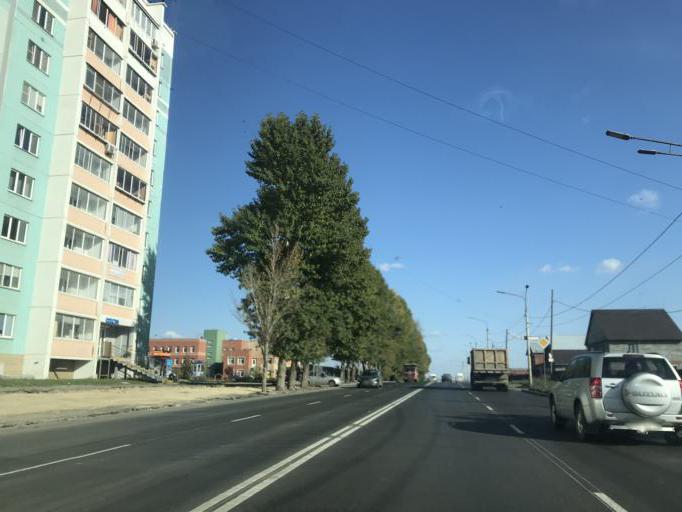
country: RU
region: Chelyabinsk
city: Roshchino
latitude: 55.2347
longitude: 61.3072
